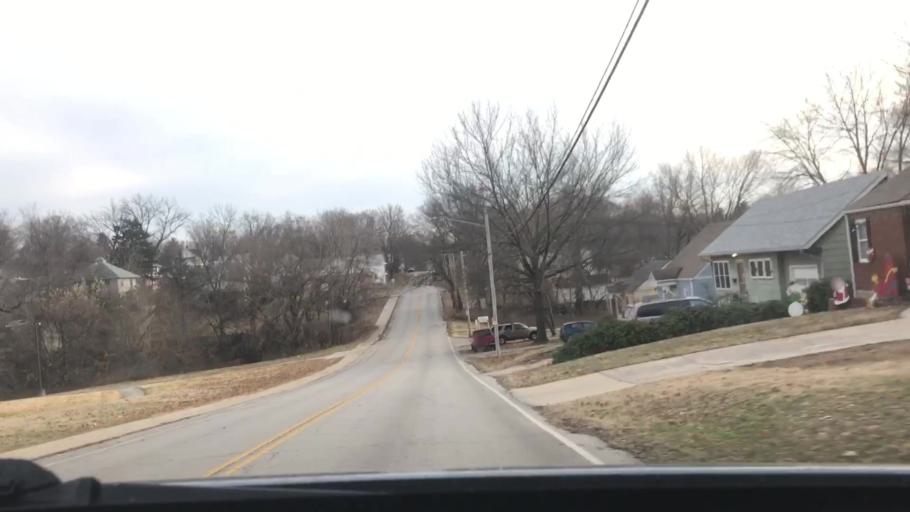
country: US
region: Missouri
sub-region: Jackson County
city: Sugar Creek
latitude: 39.0925
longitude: -94.4365
